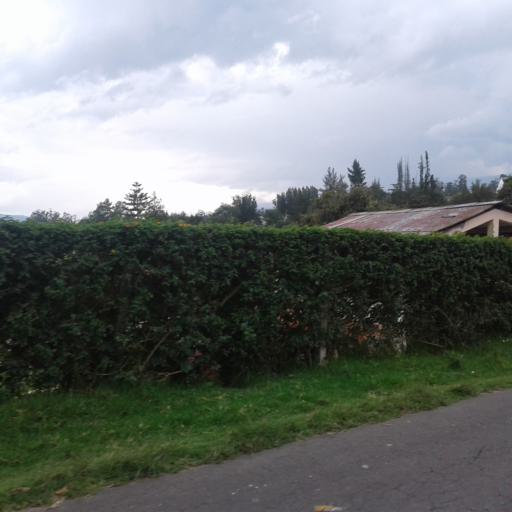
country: EC
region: Pichincha
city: Sangolqui
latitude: -0.2916
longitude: -78.3951
